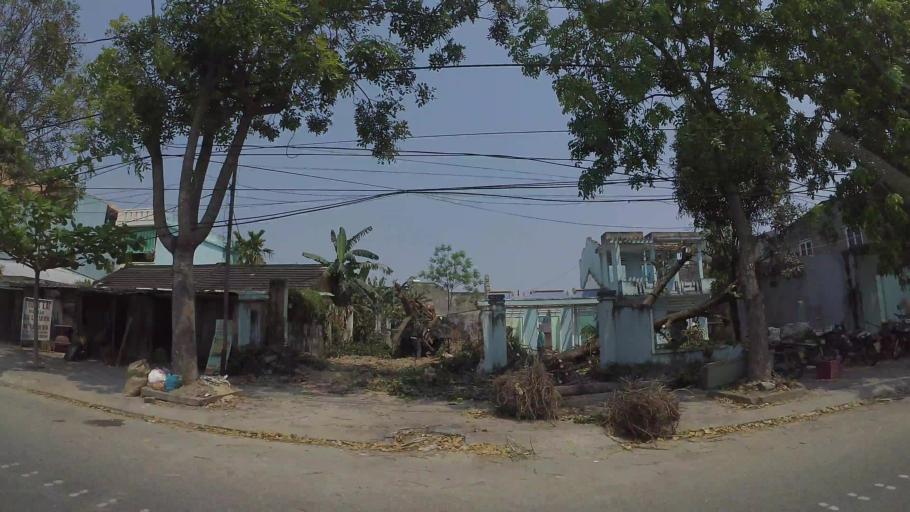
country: VN
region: Da Nang
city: Cam Le
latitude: 15.9764
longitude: 108.2085
